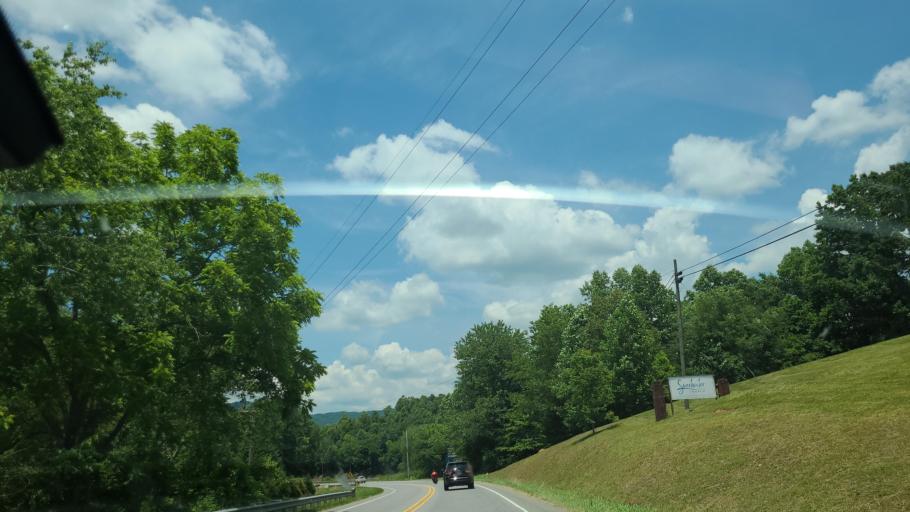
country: US
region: North Carolina
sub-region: Clay County
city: Hayesville
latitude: 35.0500
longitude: -83.8830
